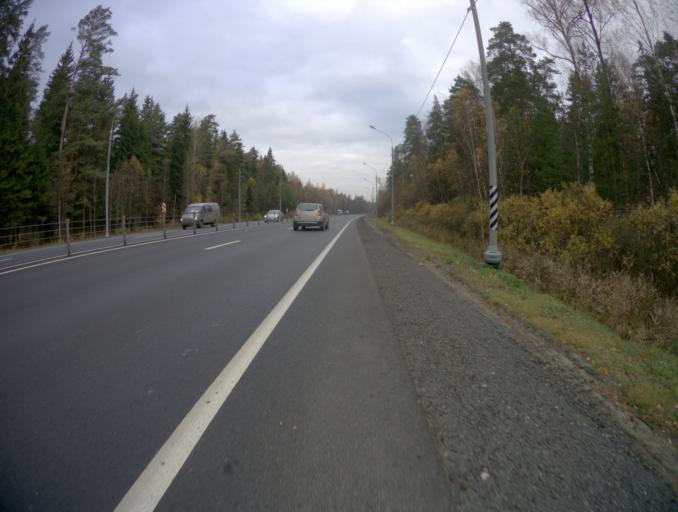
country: RU
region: Moskovskaya
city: Malaya Dubna
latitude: 55.8545
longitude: 38.9628
